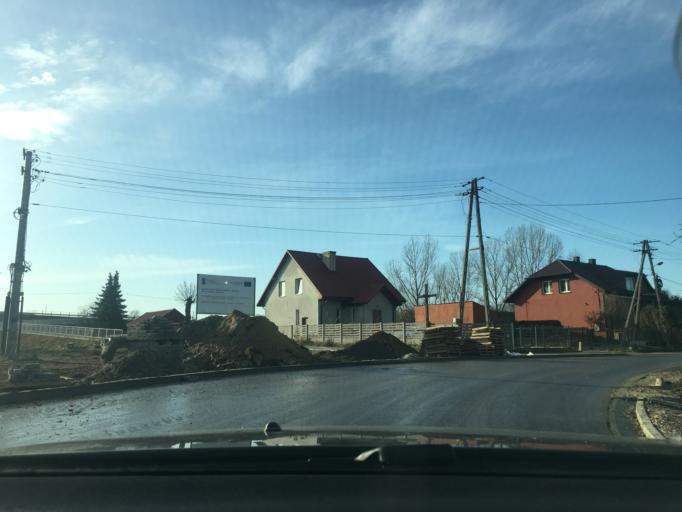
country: PL
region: Swietokrzyskie
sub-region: Powiat jedrzejowski
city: Jedrzejow
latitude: 50.6614
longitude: 20.3313
